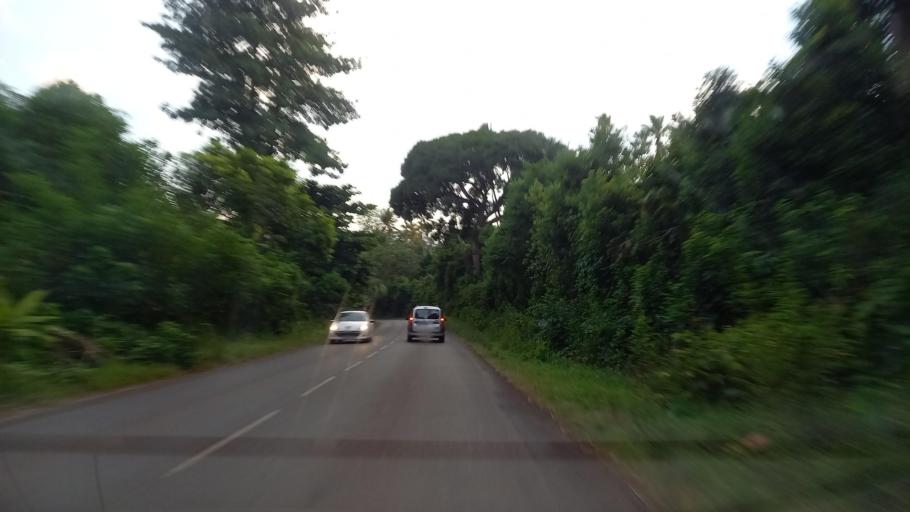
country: YT
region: M'Tsangamouji
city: M'Tsangamouji
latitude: -12.7528
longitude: 45.0926
